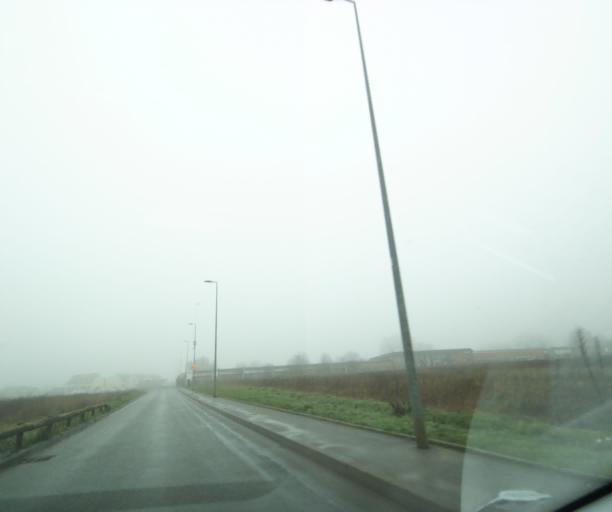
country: FR
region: Ile-de-France
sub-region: Departement de Seine-et-Marne
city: Longperrier
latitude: 49.0490
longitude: 2.6615
